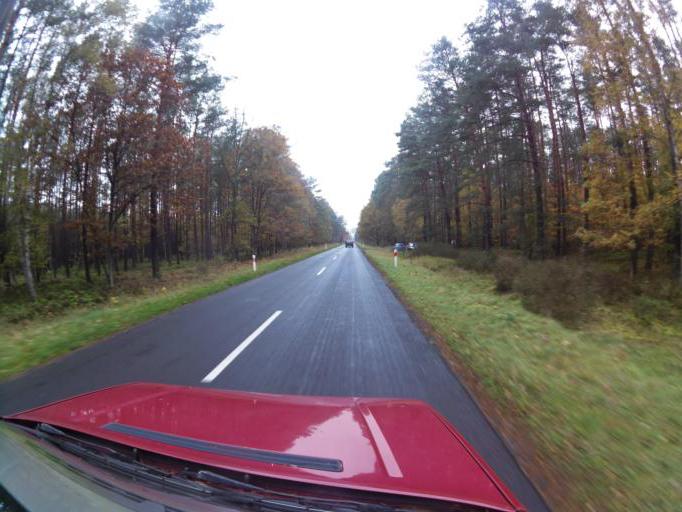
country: PL
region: West Pomeranian Voivodeship
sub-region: Powiat policki
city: Dobra
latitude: 53.5665
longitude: 14.4409
